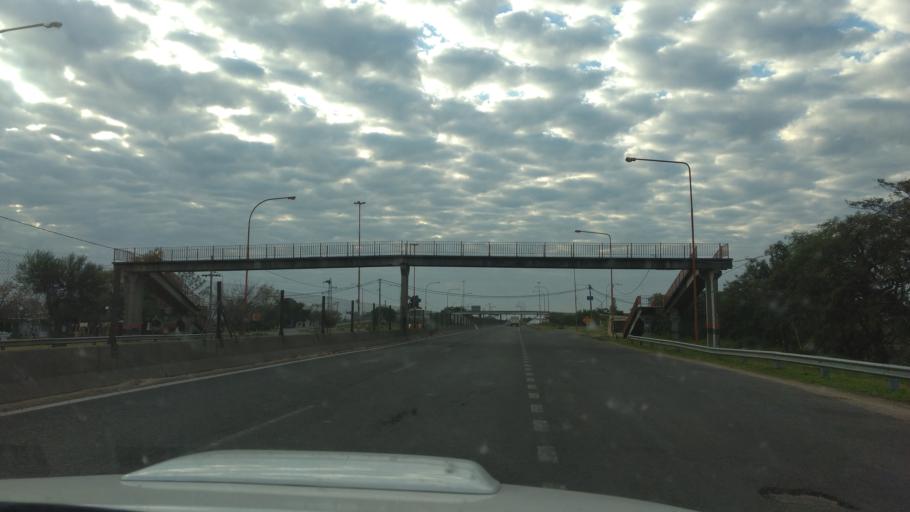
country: AR
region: Santa Fe
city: Santa Fe de la Vera Cruz
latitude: -31.6402
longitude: -60.6623
